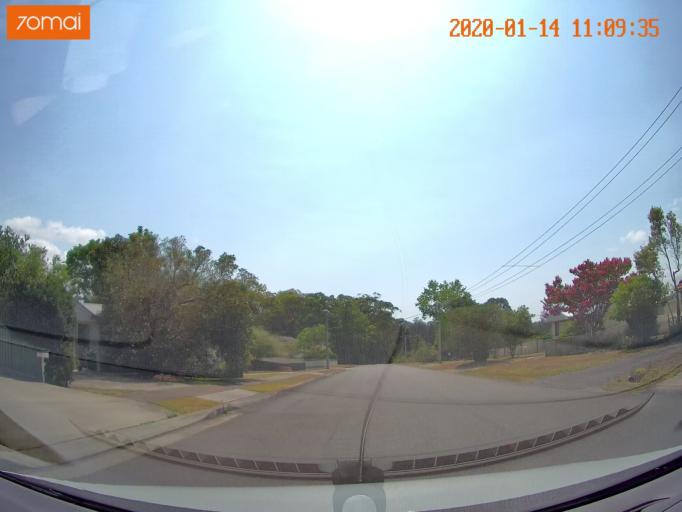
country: AU
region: New South Wales
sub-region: Lake Macquarie Shire
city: Dora Creek
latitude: -33.0961
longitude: 151.4765
